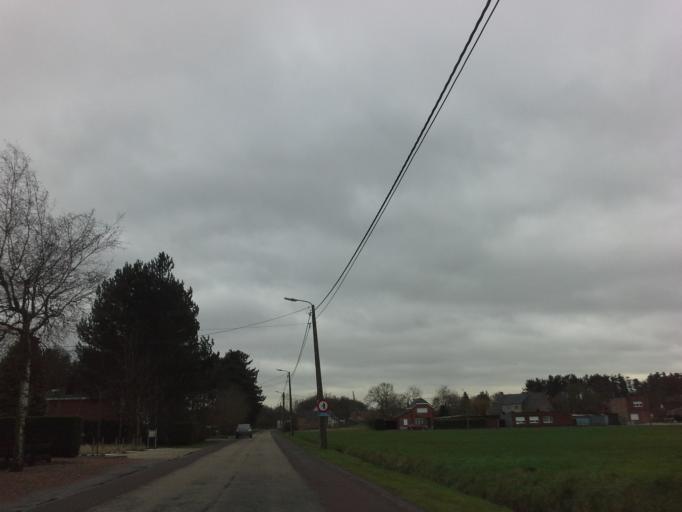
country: BE
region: Flanders
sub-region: Provincie Antwerpen
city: Hulshout
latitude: 51.0861
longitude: 4.7800
